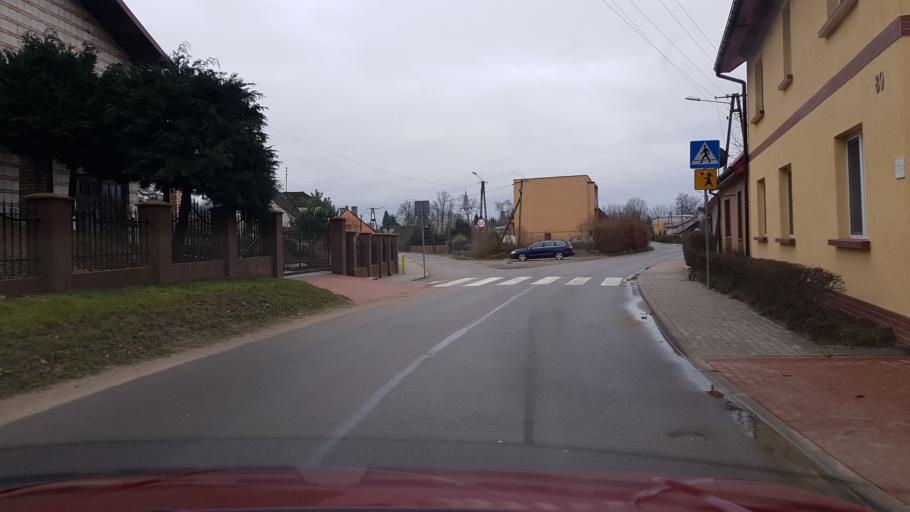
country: PL
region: West Pomeranian Voivodeship
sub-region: Powiat koszalinski
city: Mielno
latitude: 54.1366
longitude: 16.0380
